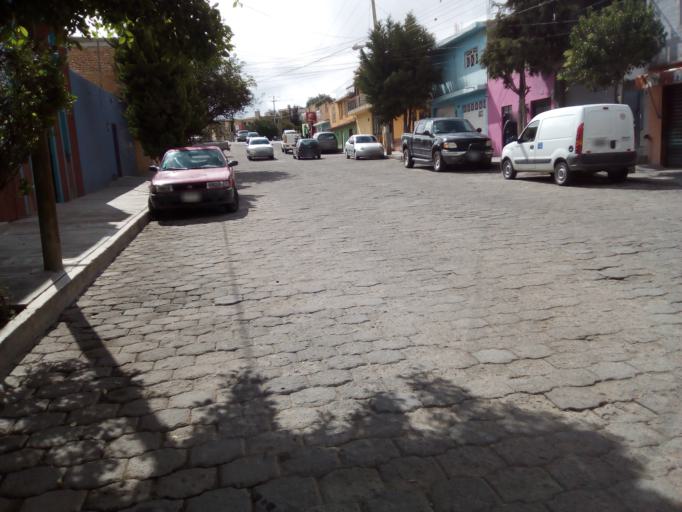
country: MX
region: Guerrero
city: San Luis de la Paz
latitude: 21.2947
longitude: -100.5112
